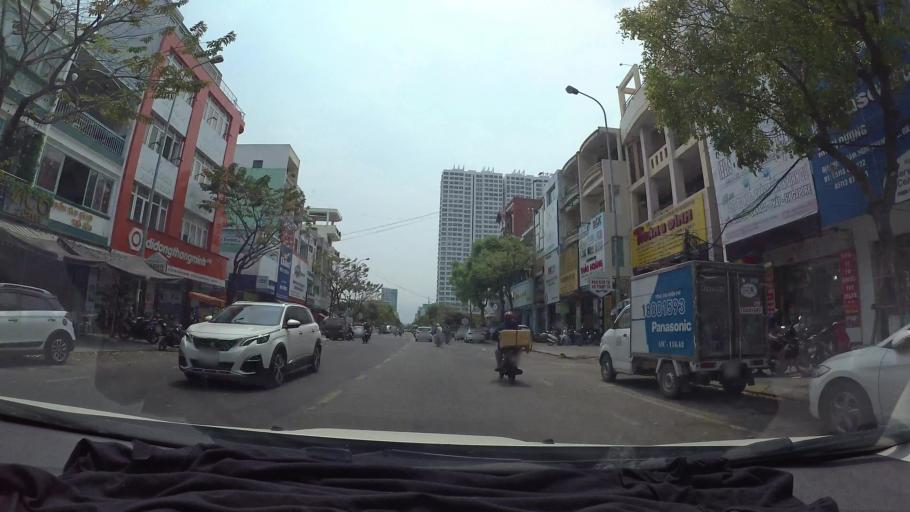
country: VN
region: Da Nang
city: Da Nang
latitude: 16.0650
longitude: 108.2104
